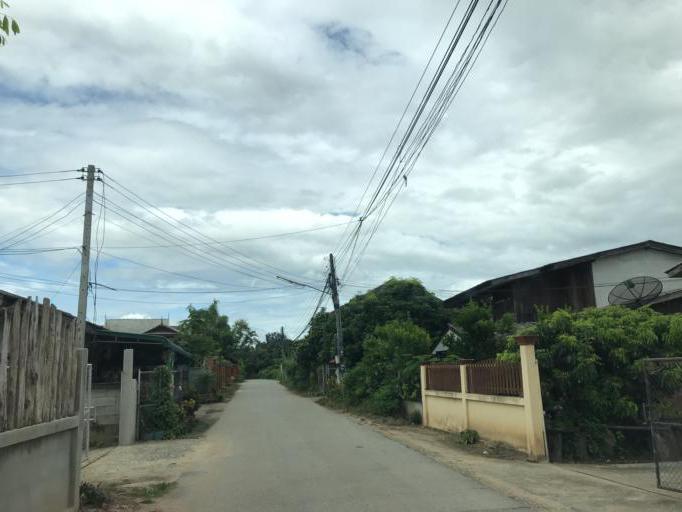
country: TH
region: Chiang Mai
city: Mae Wang
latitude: 18.5649
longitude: 98.8296
